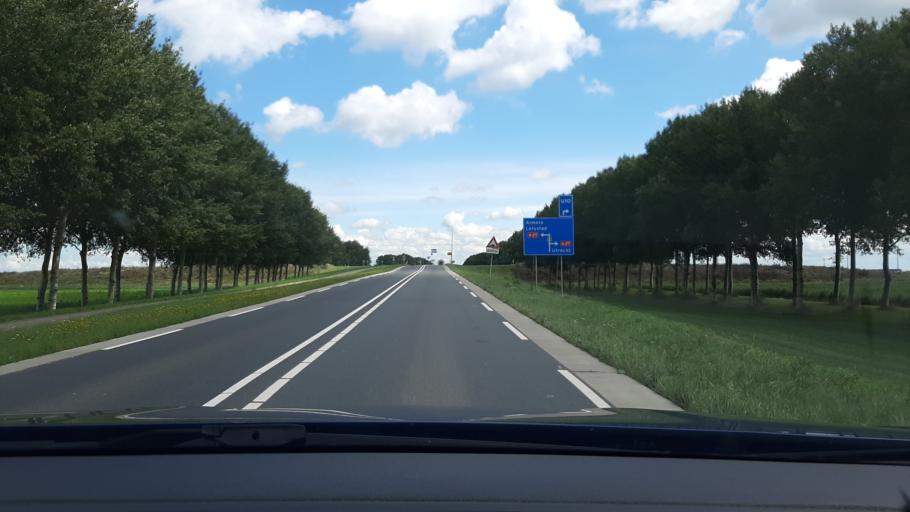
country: NL
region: North Holland
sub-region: Gemeente Huizen
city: Huizen
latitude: 52.3482
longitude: 5.3328
